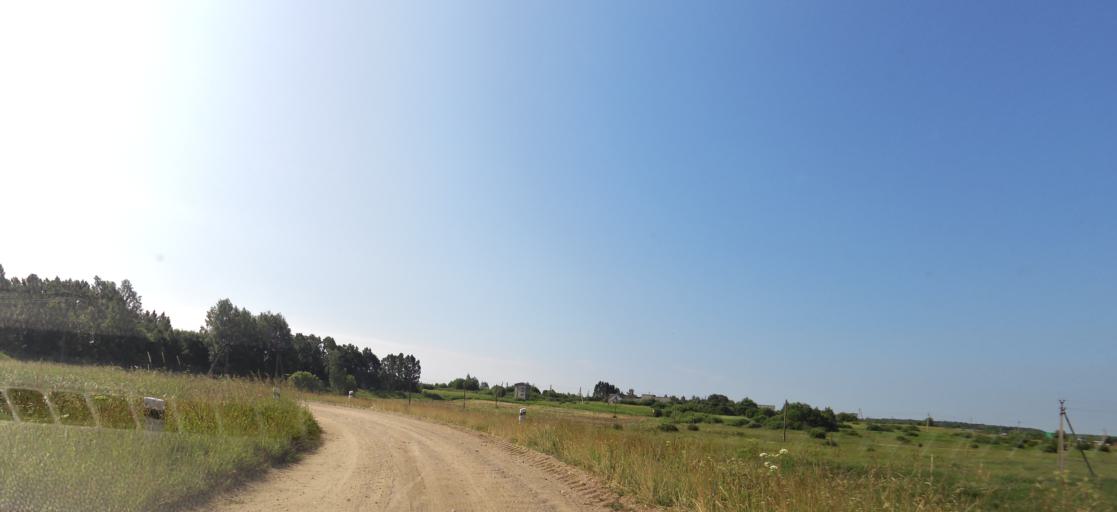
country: LT
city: Grigiskes
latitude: 54.8640
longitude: 25.0617
